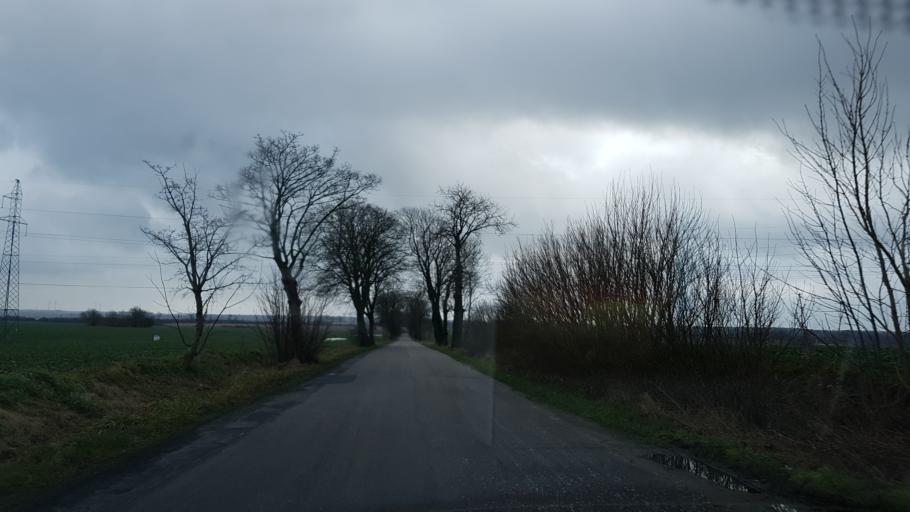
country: PL
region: West Pomeranian Voivodeship
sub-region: Powiat slawienski
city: Slawno
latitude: 54.4825
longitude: 16.7246
